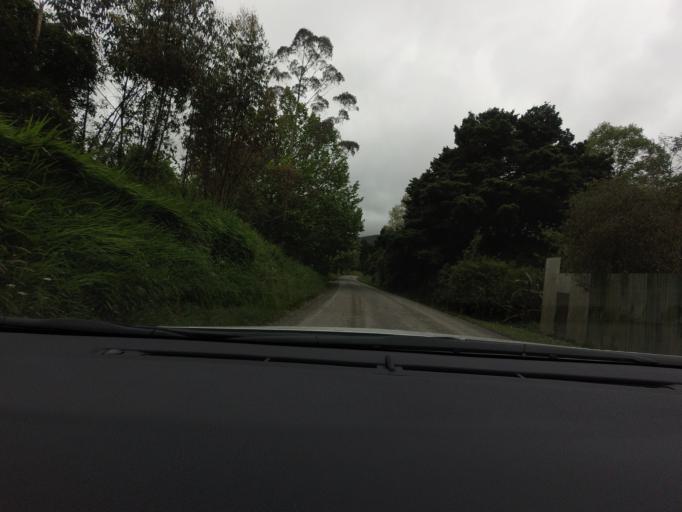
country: NZ
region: Auckland
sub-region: Auckland
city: Warkworth
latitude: -36.4775
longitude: 174.5558
